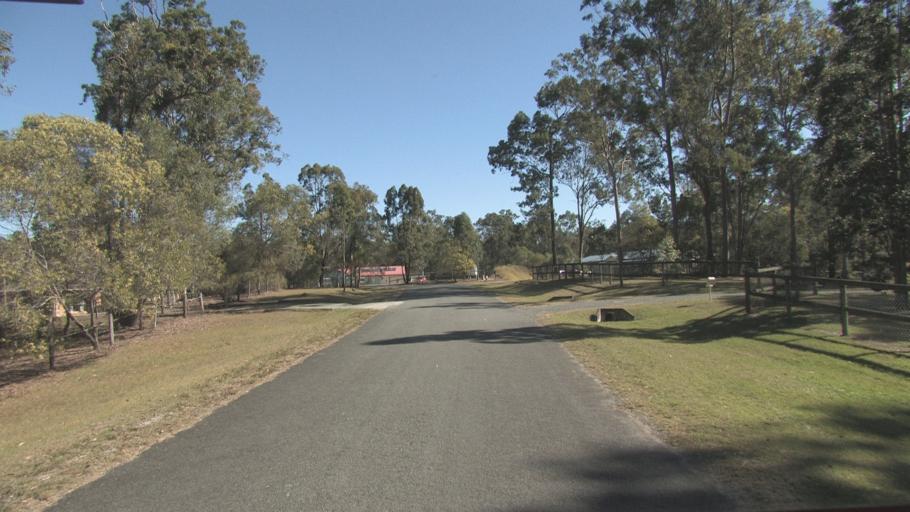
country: AU
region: Queensland
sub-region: Ipswich
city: Springfield Lakes
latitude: -27.7163
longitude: 152.9291
